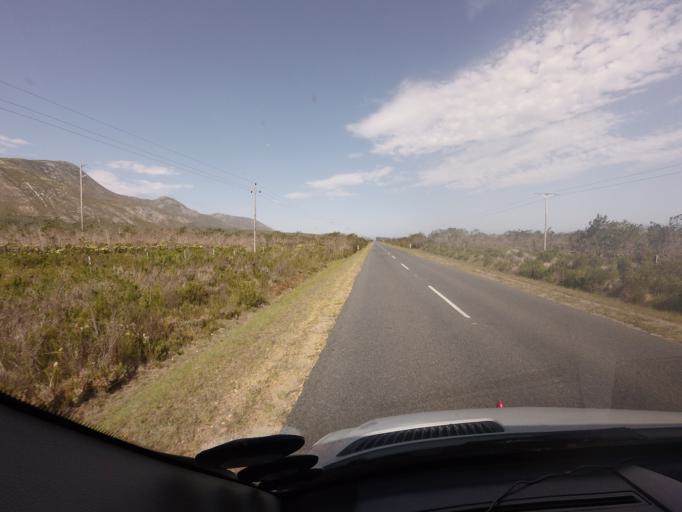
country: ZA
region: Western Cape
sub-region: Overberg District Municipality
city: Hermanus
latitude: -34.4086
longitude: 19.3925
